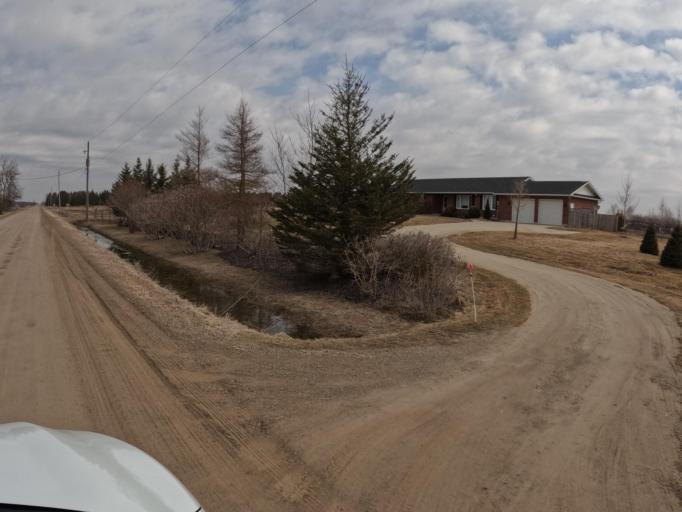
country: CA
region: Ontario
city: Orangeville
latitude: 43.9105
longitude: -80.2155
